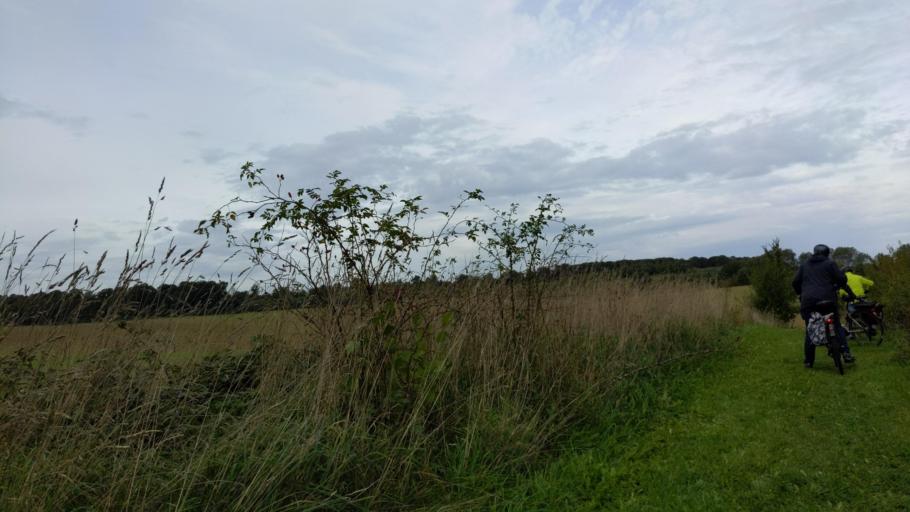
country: DE
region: Schleswig-Holstein
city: Mechow
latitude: 53.7293
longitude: 10.8058
